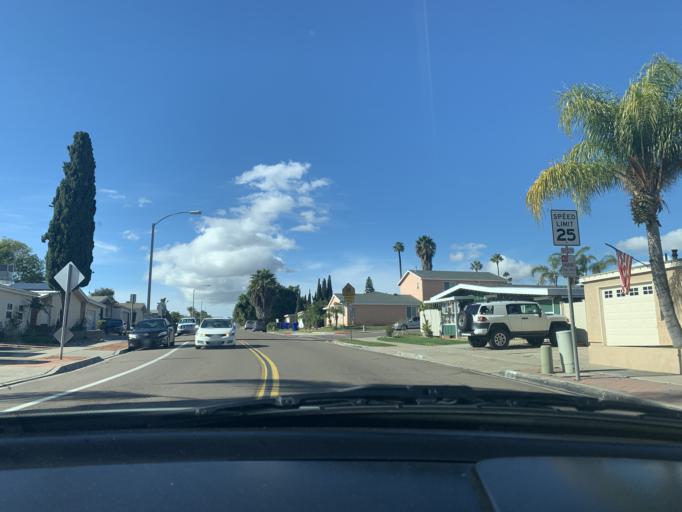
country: US
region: California
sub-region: San Diego County
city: San Diego
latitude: 32.8045
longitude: -117.1360
